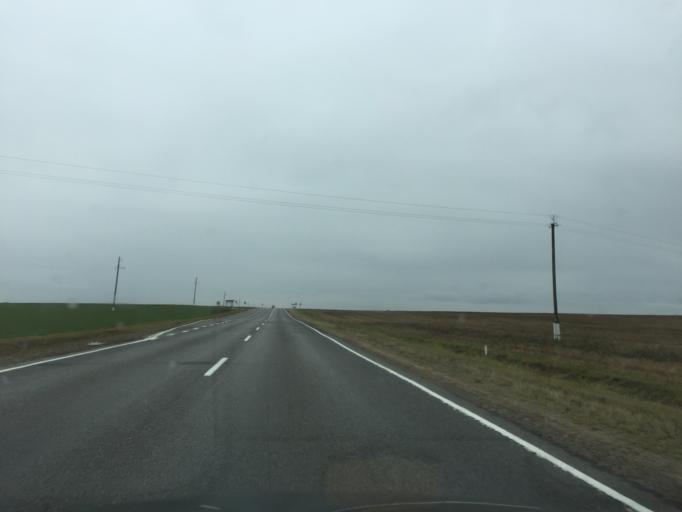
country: BY
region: Mogilev
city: Cherykaw
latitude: 53.6210
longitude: 31.2996
